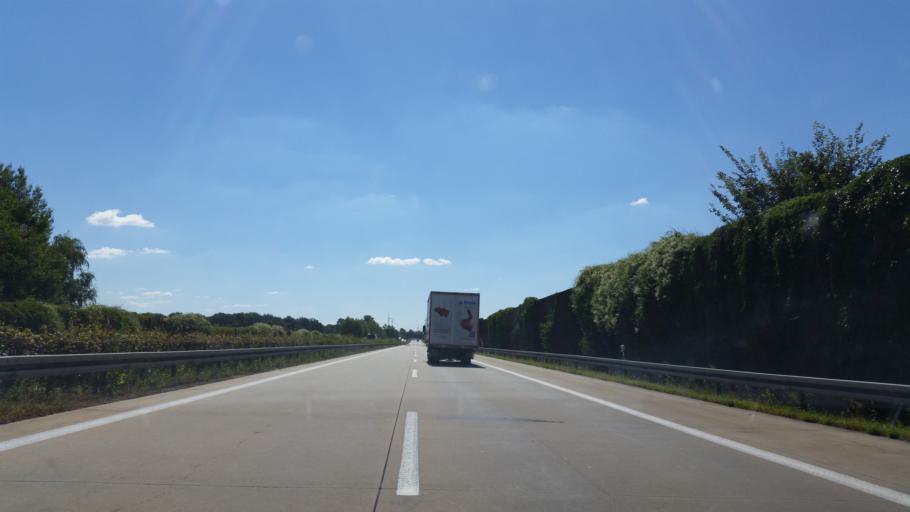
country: DE
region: Brandenburg
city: Vetschau
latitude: 51.7995
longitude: 14.0460
